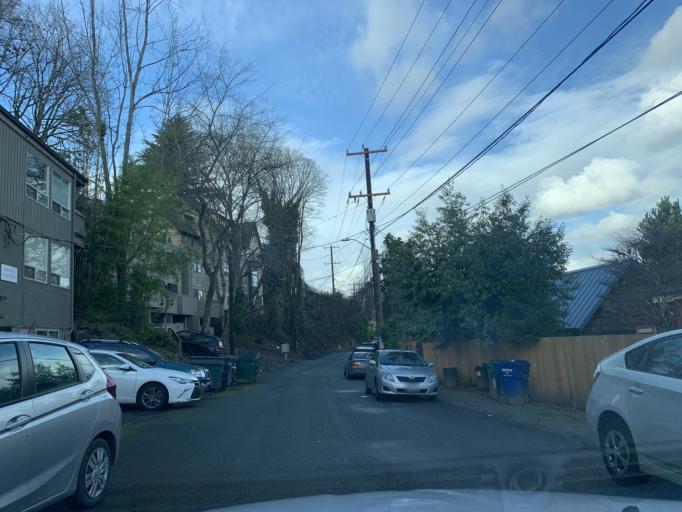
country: US
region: Washington
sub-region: King County
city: Seattle
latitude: 47.6640
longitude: -122.3033
